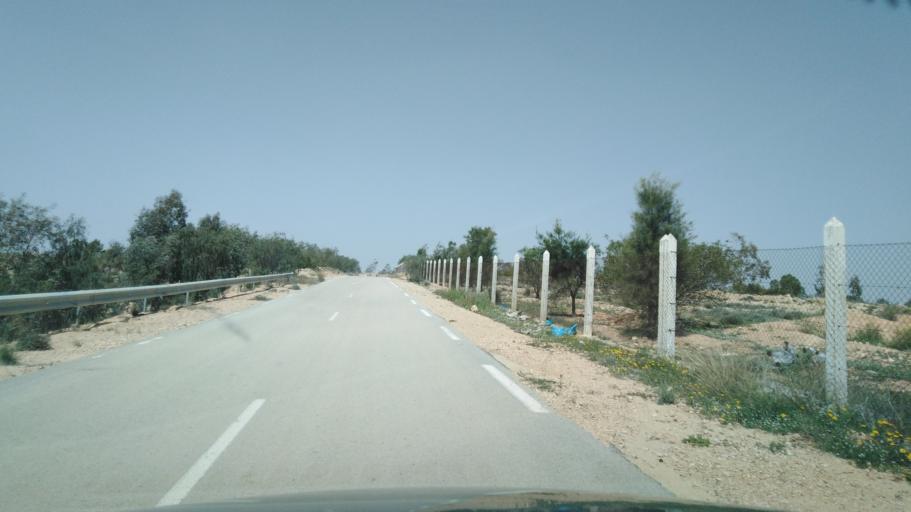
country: TN
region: Safaqis
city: Sfax
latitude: 34.7070
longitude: 10.5244
